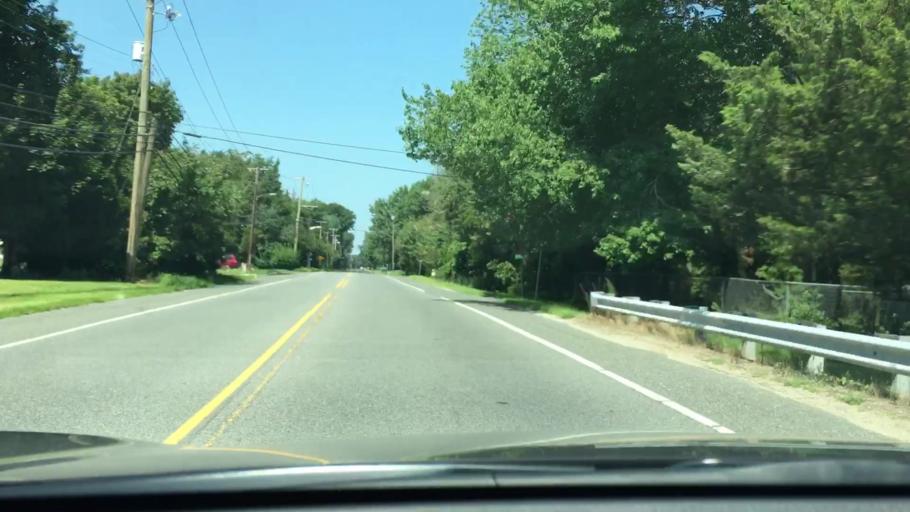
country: US
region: New Jersey
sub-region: Cumberland County
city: Laurel Lake
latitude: 39.3344
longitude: -75.0209
